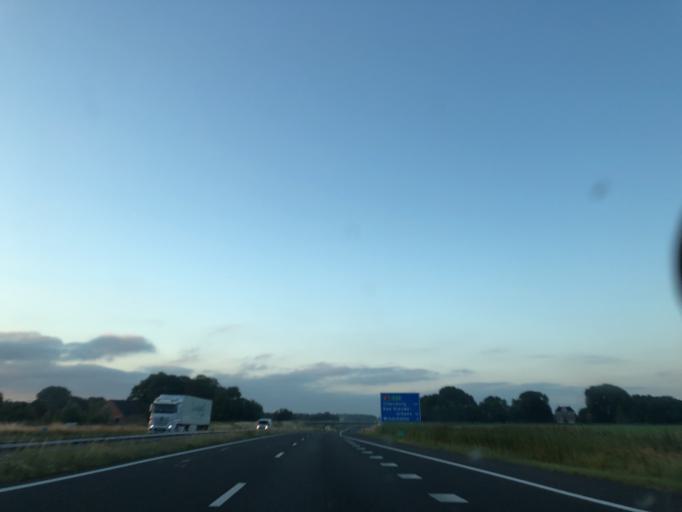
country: NL
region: Groningen
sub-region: Gemeente  Oldambt
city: Winschoten
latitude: 53.1848
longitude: 6.9771
